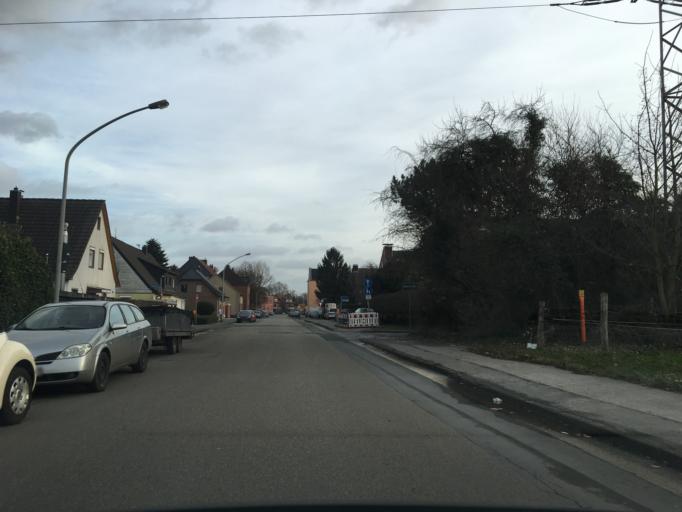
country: DE
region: North Rhine-Westphalia
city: Meiderich
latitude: 51.5121
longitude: 6.8071
